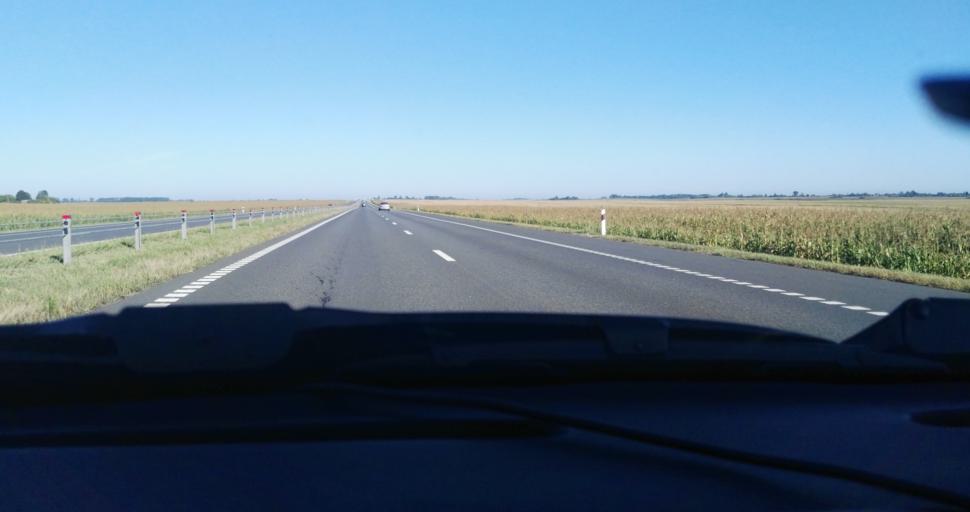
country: BY
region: Gomel
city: Buda-Kashalyova
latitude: 52.5262
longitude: 30.6156
